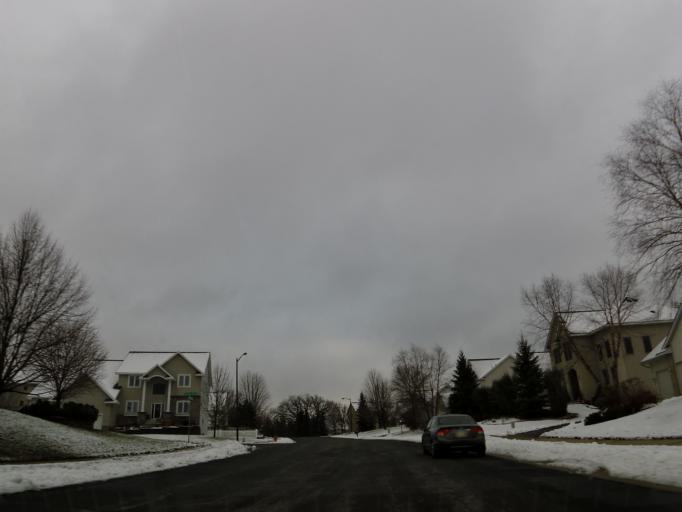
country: US
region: Minnesota
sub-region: Dakota County
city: Apple Valley
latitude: 44.7122
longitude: -93.2511
